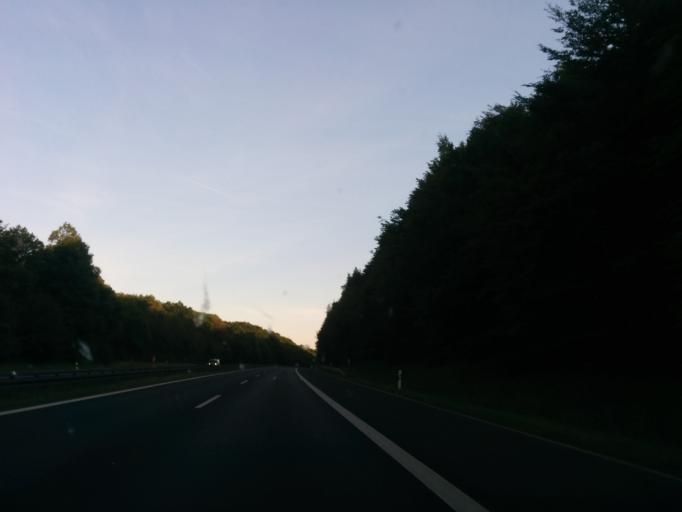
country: DE
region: Bavaria
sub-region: Regierungsbezirk Unterfranken
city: Unterpleichfeld
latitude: 49.9009
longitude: 10.0010
